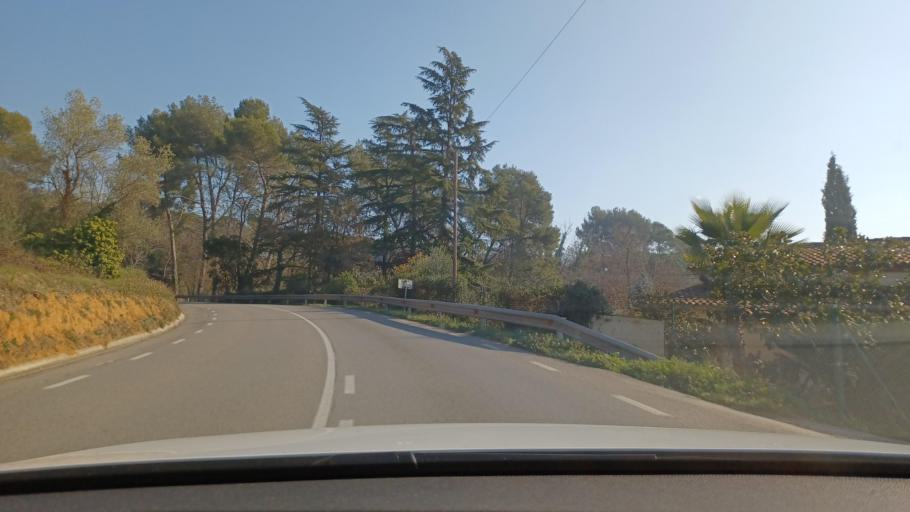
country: ES
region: Catalonia
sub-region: Provincia de Barcelona
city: Santa Eulalia de Roncana
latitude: 41.6637
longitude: 2.2366
